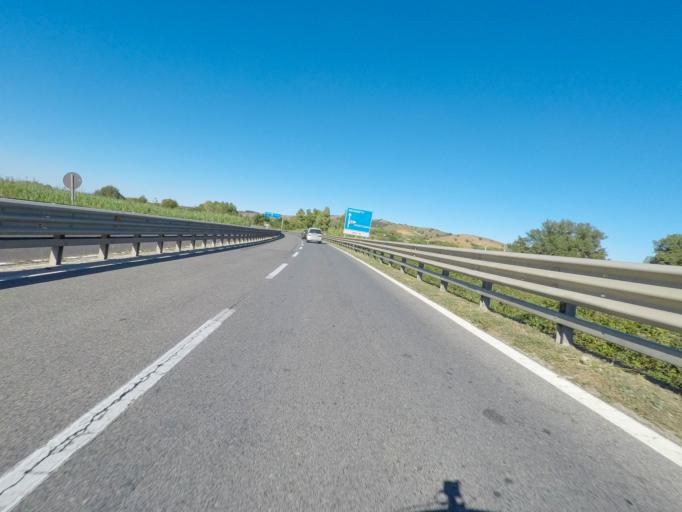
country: IT
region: Tuscany
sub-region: Provincia di Grosseto
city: Grosseto
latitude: 42.7113
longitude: 11.1444
